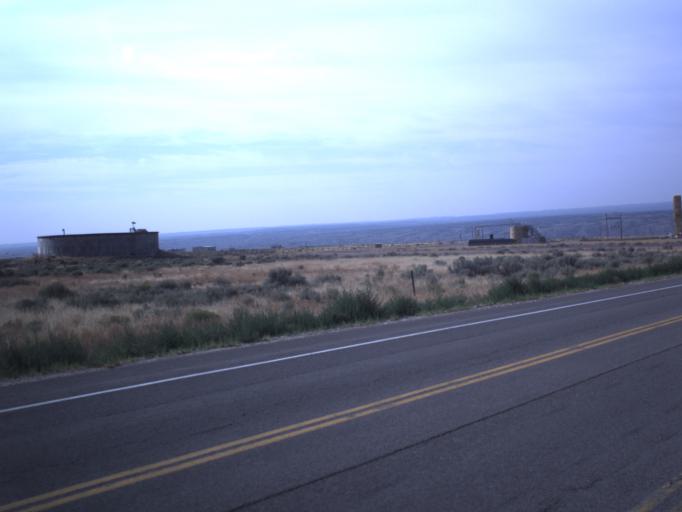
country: US
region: Utah
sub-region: Duchesne County
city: Duchesne
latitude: 40.1983
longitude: -110.3901
